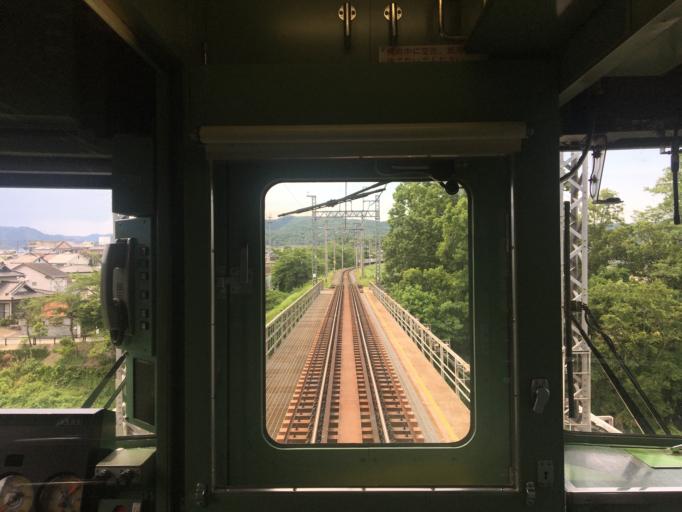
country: JP
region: Saitama
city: Yorii
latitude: 36.1153
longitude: 139.2028
